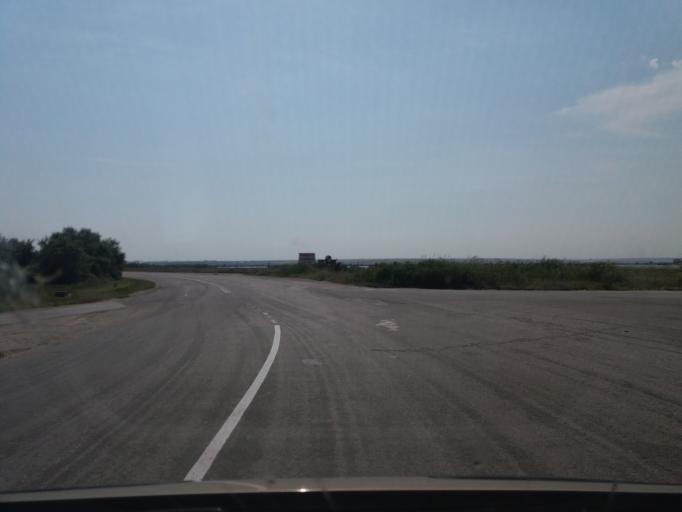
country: RO
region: Constanta
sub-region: Comuna Corbu
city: Corbu
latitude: 44.3517
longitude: 28.6496
